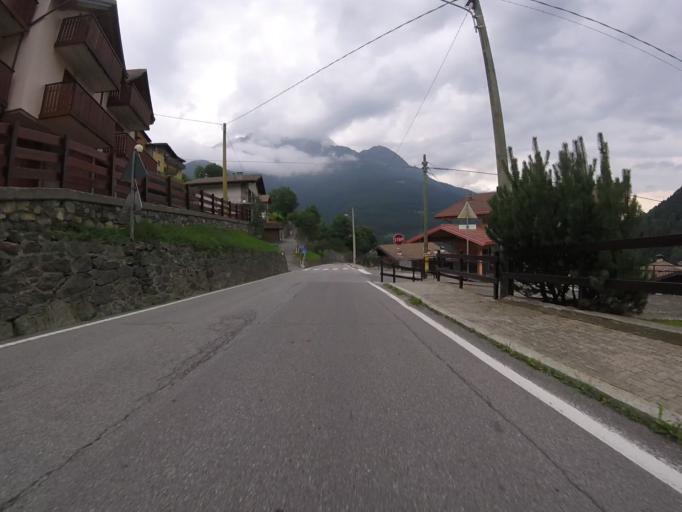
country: IT
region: Lombardy
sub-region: Provincia di Brescia
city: Monno
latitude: 46.2119
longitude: 10.3428
